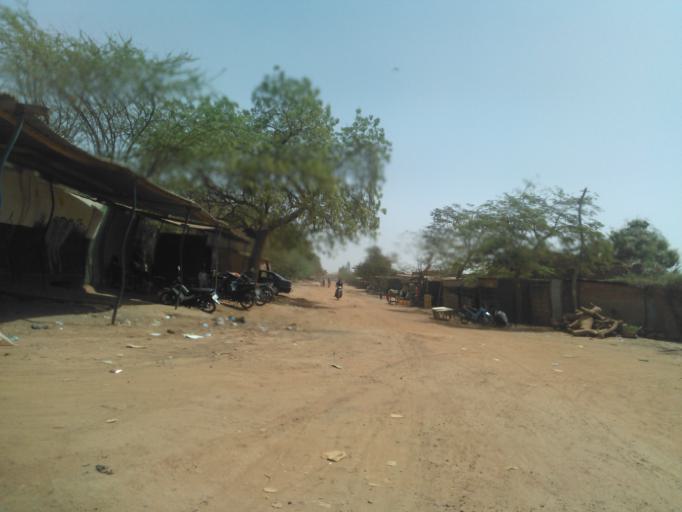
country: BF
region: Centre
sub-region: Kadiogo Province
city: Ouagadougou
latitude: 12.3929
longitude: -1.5720
